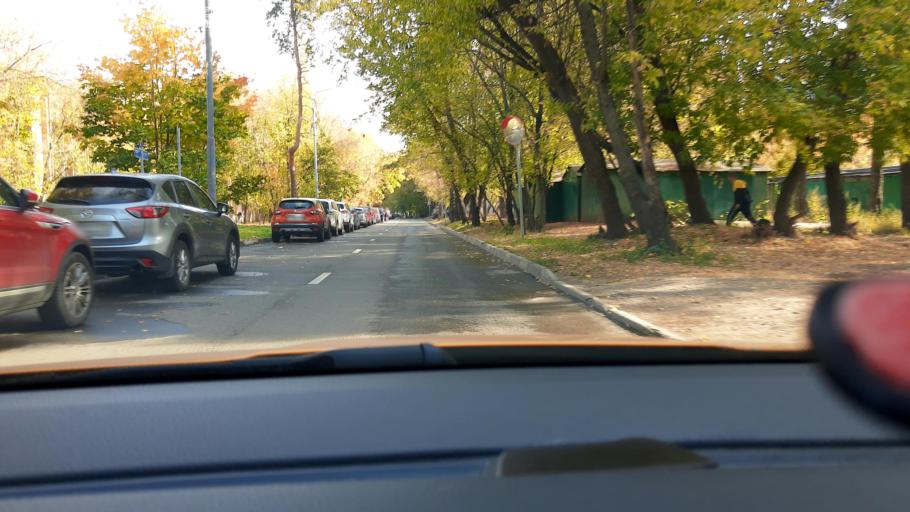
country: RU
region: Moscow
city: Leonovo
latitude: 55.8572
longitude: 37.6484
